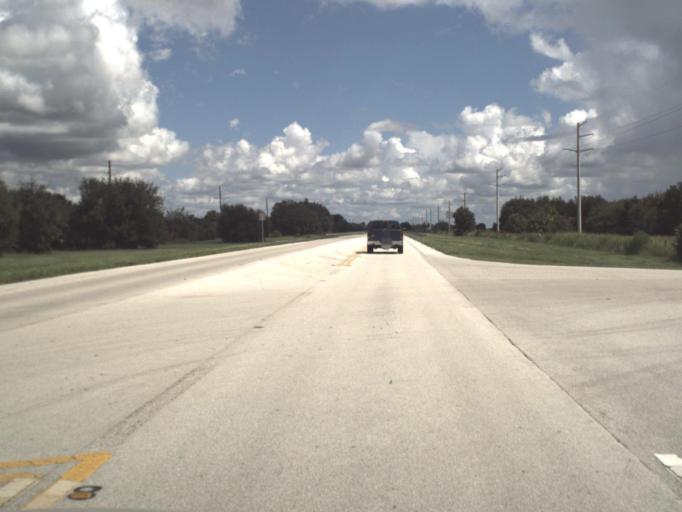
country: US
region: Florida
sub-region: DeSoto County
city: Southeast Arcadia
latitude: 27.2095
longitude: -81.6566
